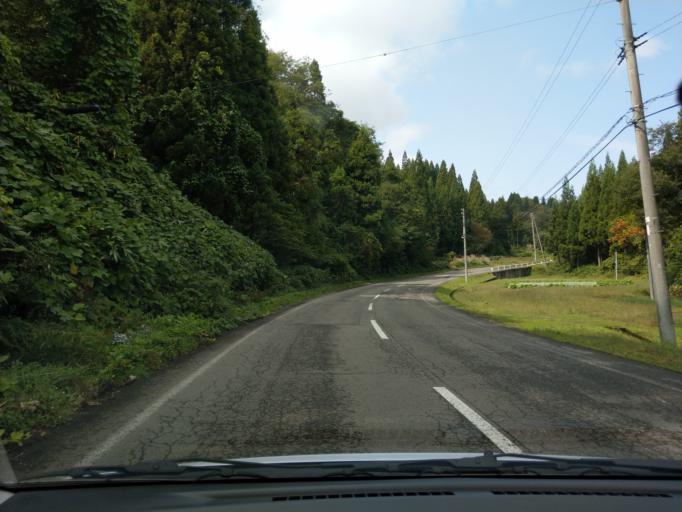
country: JP
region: Akita
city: Omagari
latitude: 39.5088
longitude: 140.3107
